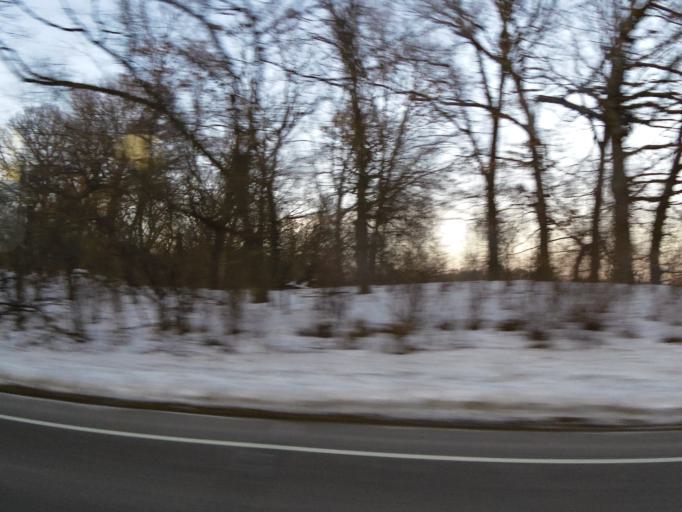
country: US
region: Minnesota
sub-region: Washington County
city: Dellwood
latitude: 45.0920
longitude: -92.9650
